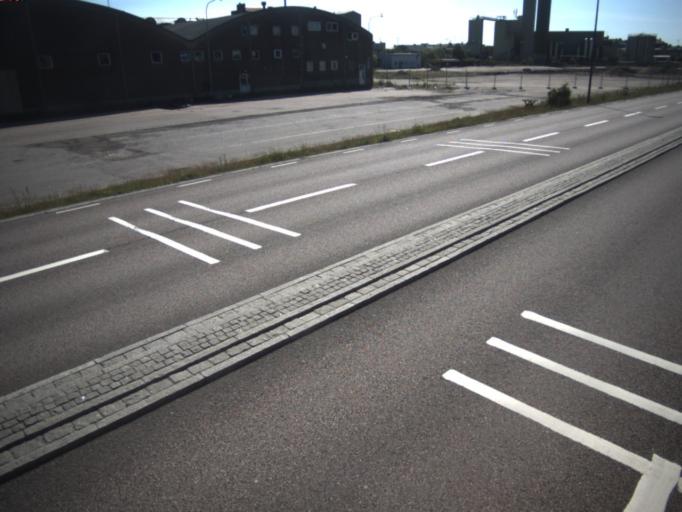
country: SE
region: Skane
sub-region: Helsingborg
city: Helsingborg
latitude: 56.0361
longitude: 12.6970
